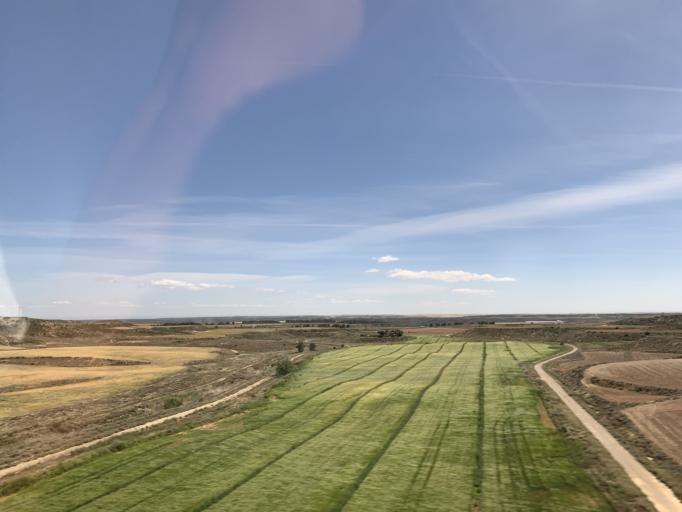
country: ES
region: Aragon
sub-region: Provincia de Huesca
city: Penalba
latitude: 41.5236
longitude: -0.0031
